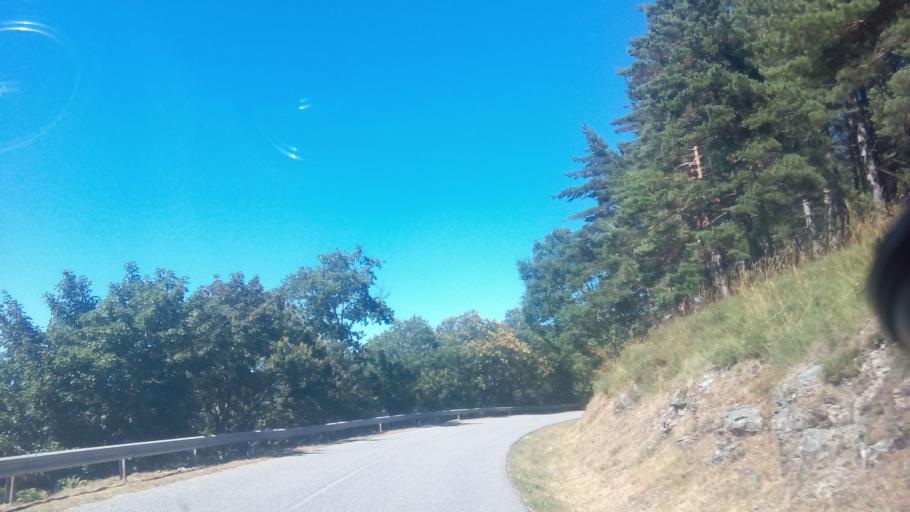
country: PT
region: Vila Real
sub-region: Santa Marta de Penaguiao
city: Santa Marta de Penaguiao
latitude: 41.2813
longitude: -7.8852
